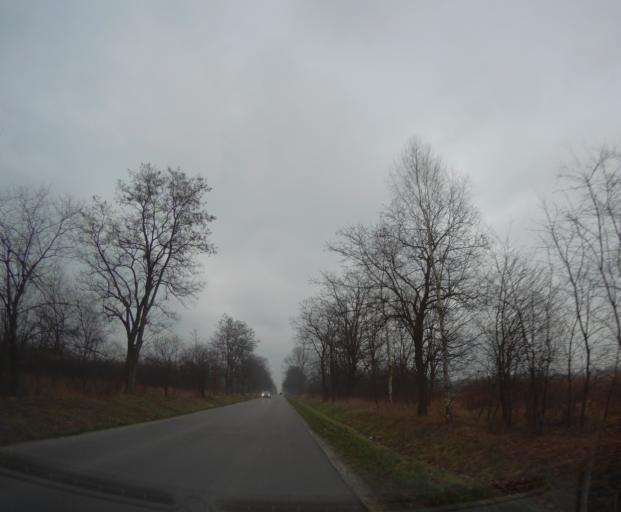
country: PL
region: Lublin Voivodeship
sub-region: Powiat bilgorajski
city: Bilgoraj
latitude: 50.5399
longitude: 22.6842
